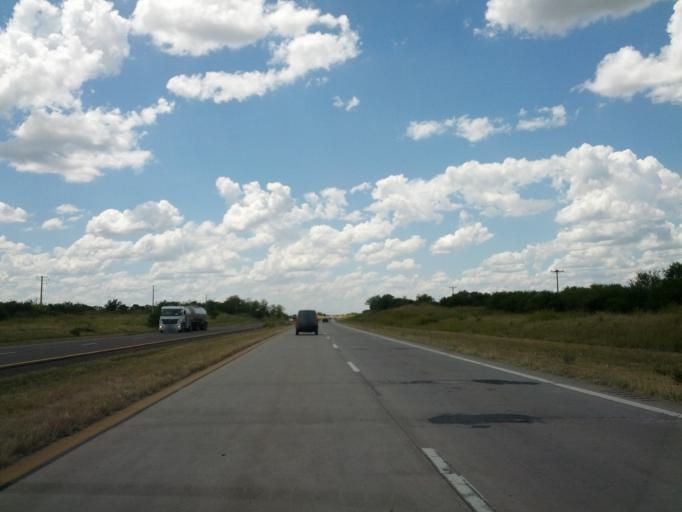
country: AR
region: Entre Rios
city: Gualeguaychu
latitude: -32.9460
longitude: -58.5783
